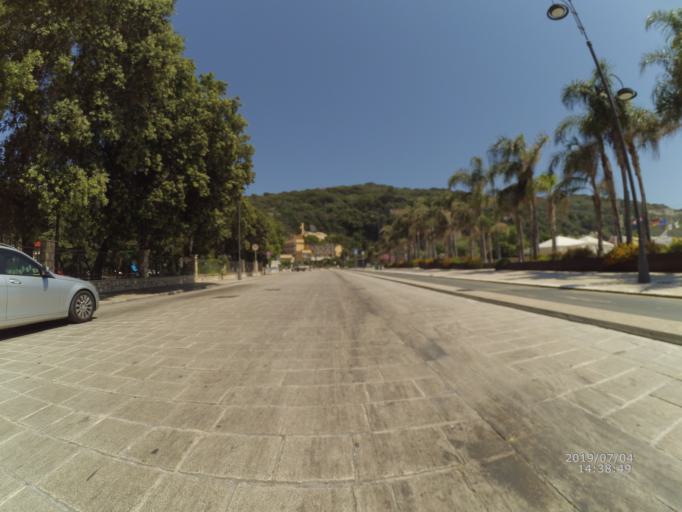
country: IT
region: Latium
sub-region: Provincia di Latina
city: Gaeta
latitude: 41.2098
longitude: 13.5698
